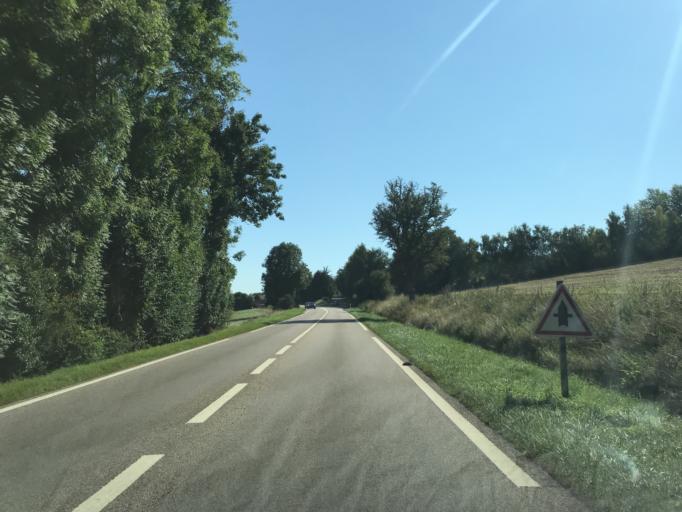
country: FR
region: Ile-de-France
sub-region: Departement du Val-d'Oise
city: Magny-en-Vexin
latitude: 49.1447
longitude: 1.7605
